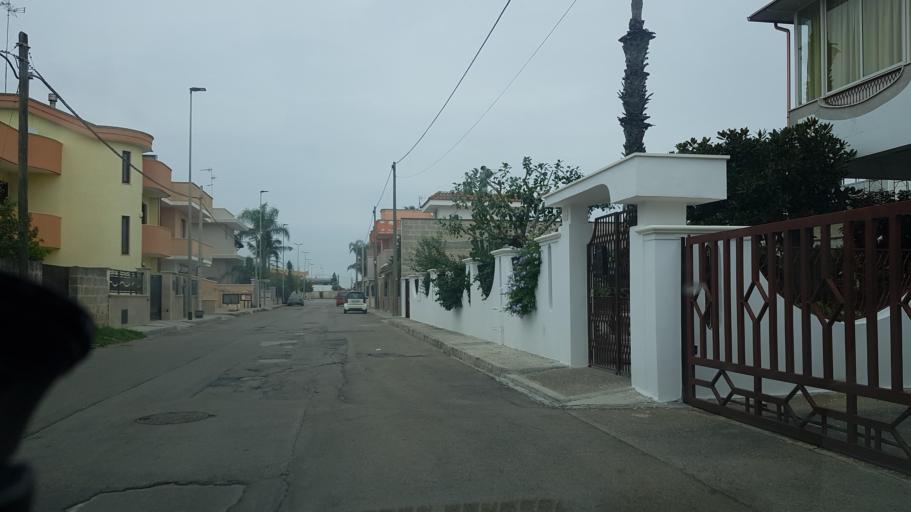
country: IT
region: Apulia
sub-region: Provincia di Lecce
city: Leverano
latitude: 40.2887
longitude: 18.0066
